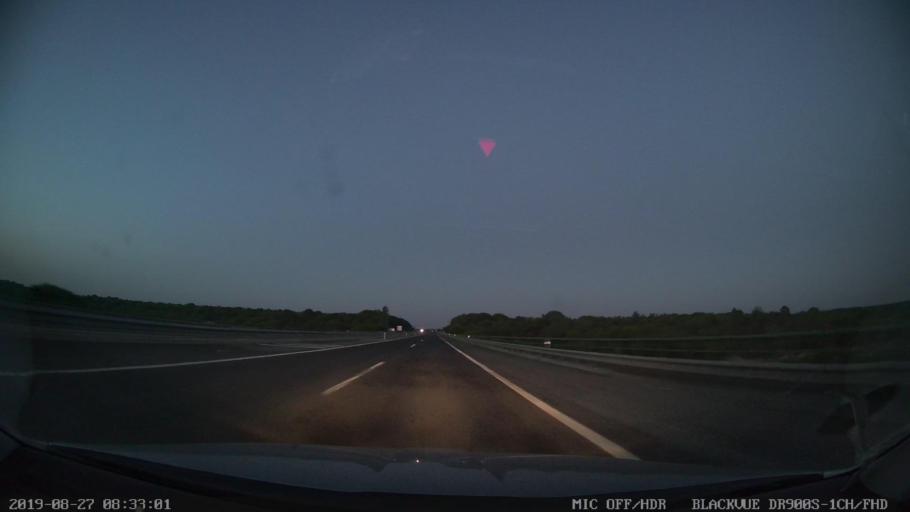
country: PT
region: Evora
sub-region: Vendas Novas
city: Vendas Novas
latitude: 38.6225
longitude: -8.5730
